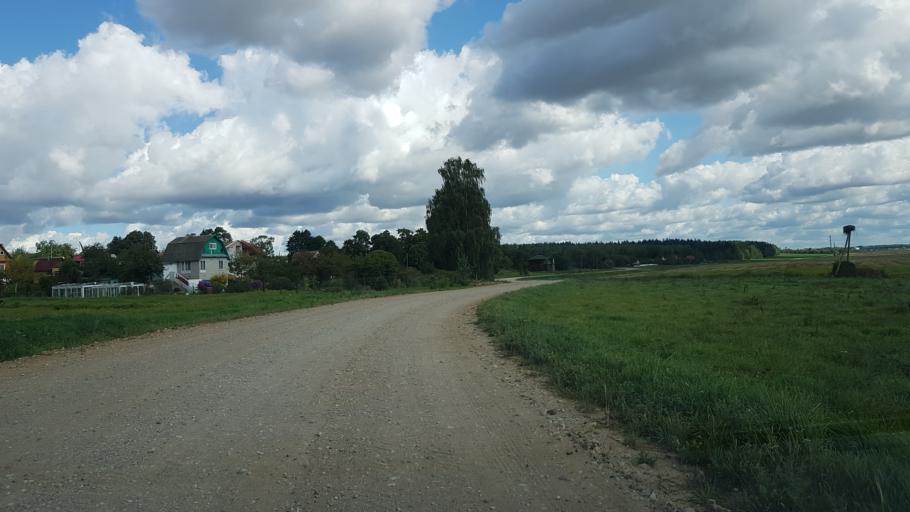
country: BY
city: Fanipol
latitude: 53.7364
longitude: 27.2564
